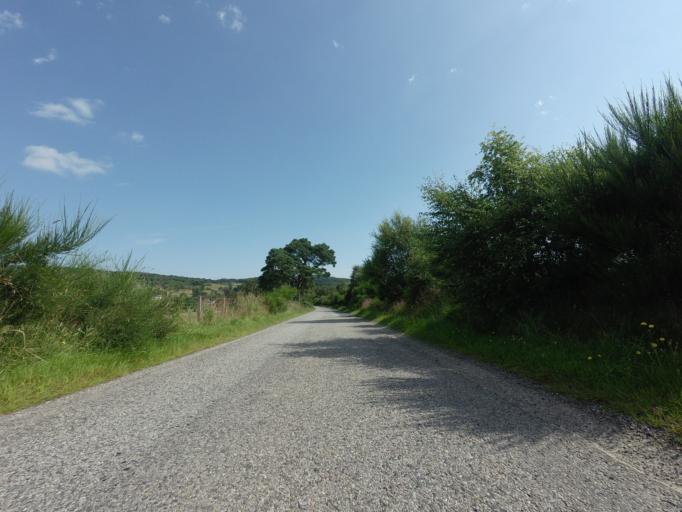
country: GB
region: Scotland
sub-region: Highland
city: Invergordon
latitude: 57.7497
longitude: -4.1615
